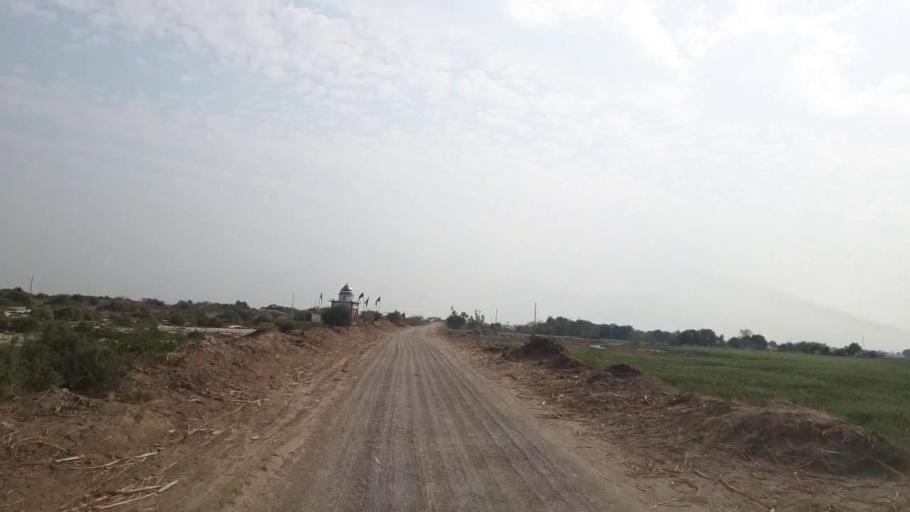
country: PK
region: Sindh
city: Mirpur Khas
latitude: 25.5568
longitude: 69.1699
